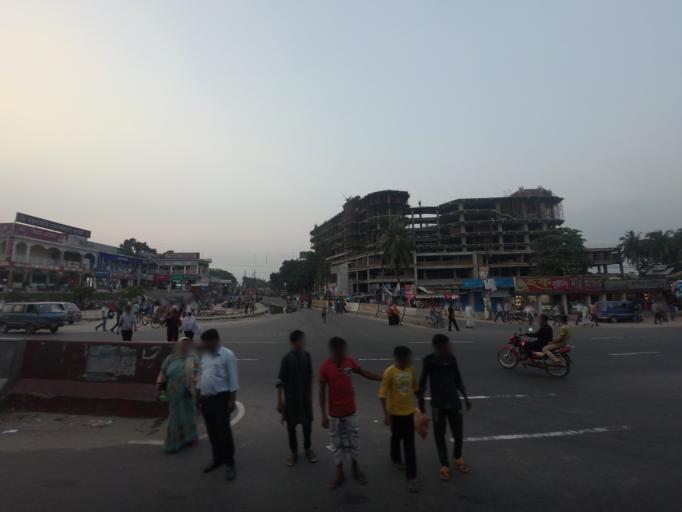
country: BD
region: Chittagong
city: Comilla
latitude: 23.4789
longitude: 91.1180
